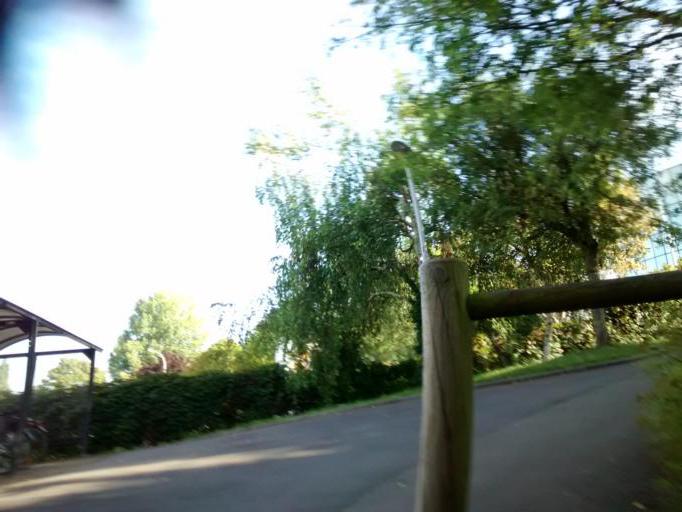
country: FR
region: Brittany
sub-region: Departement d'Ille-et-Vilaine
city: Cesson-Sevigne
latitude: 48.1126
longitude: -1.6025
